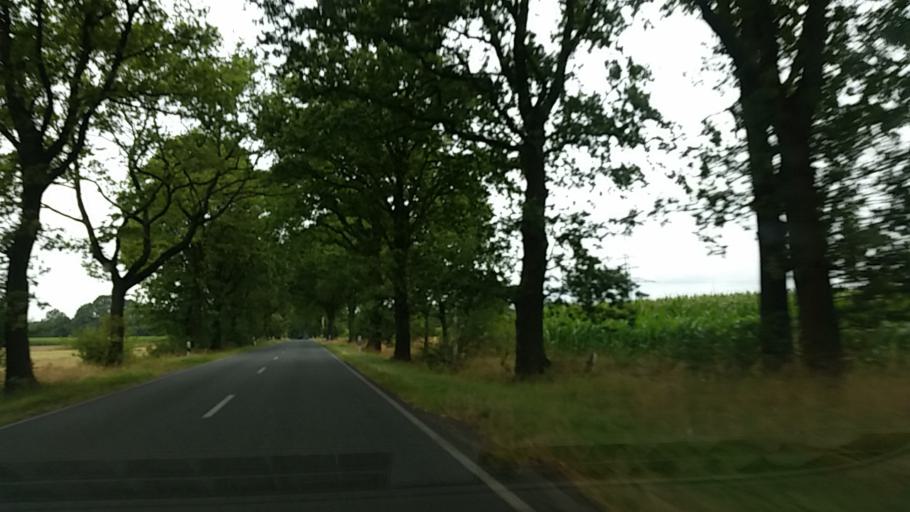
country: DE
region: Lower Saxony
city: Vollersode
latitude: 53.4060
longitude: 8.9189
